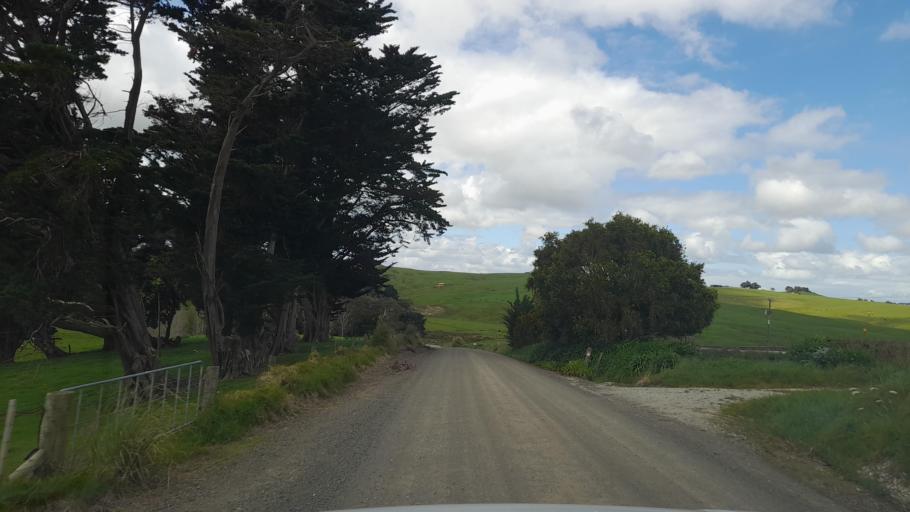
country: NZ
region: Auckland
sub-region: Auckland
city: Wellsford
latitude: -36.1909
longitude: 174.3258
